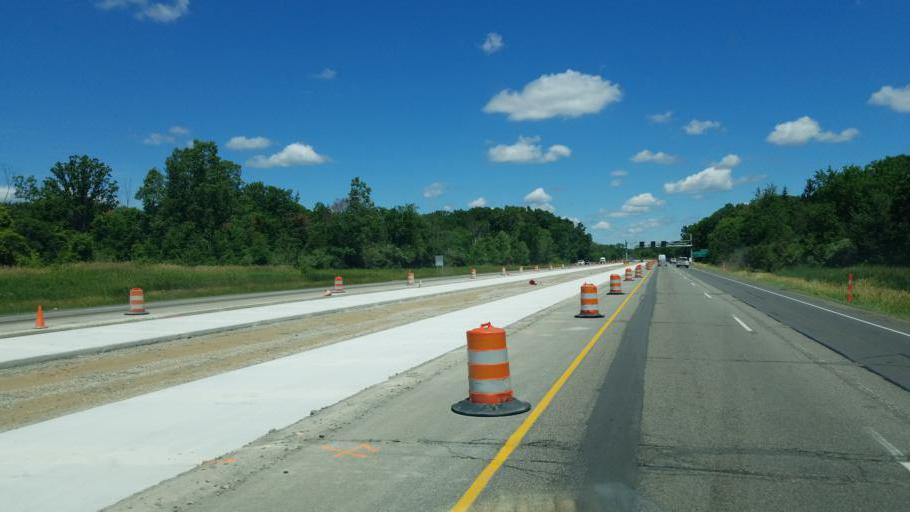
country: US
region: Michigan
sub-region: Livingston County
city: Whitmore Lake
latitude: 42.3613
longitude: -83.7489
